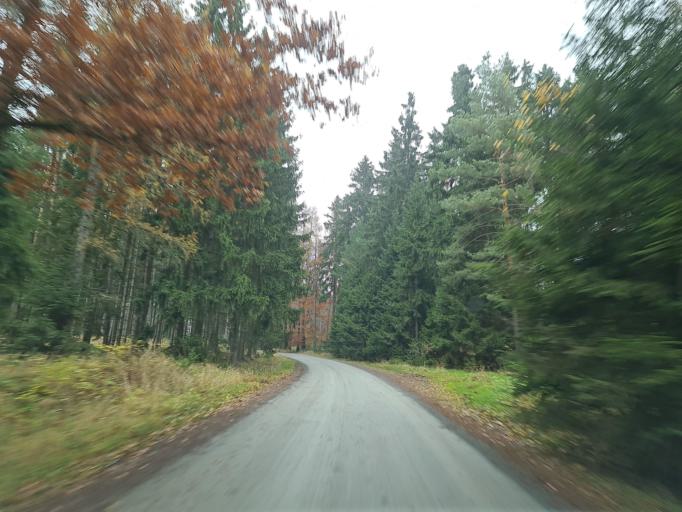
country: DE
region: Saxony
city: Mehltheuer
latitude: 50.5259
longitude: 12.0479
